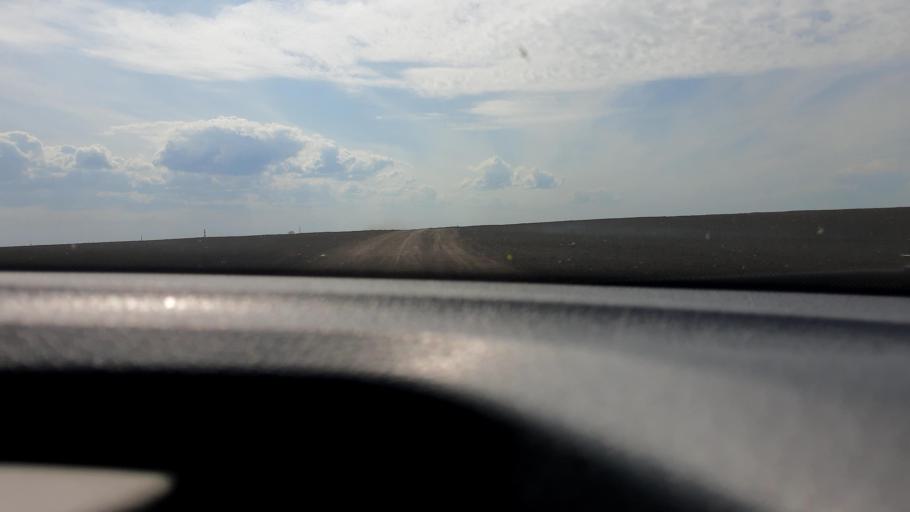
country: RU
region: Bashkortostan
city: Avdon
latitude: 54.7150
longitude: 55.7868
